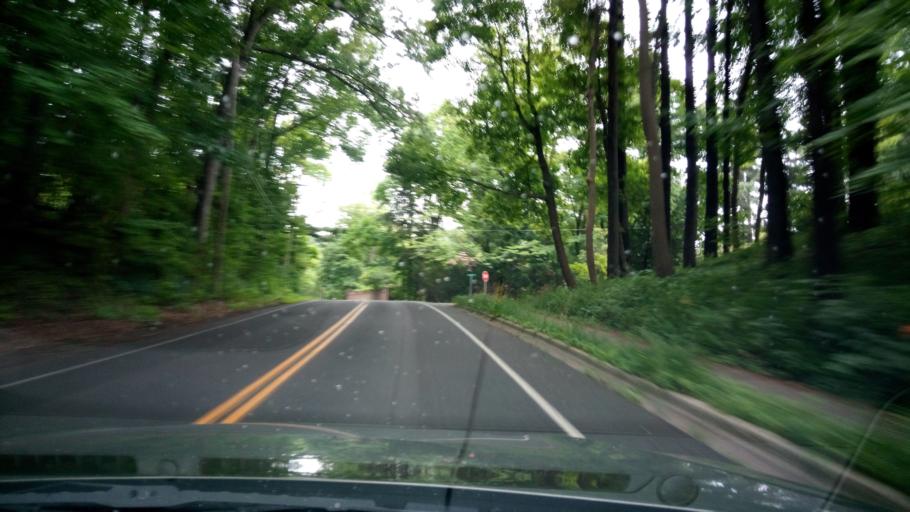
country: US
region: New York
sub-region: Tompkins County
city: Cayuga Heights
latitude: 42.4617
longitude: -76.4830
